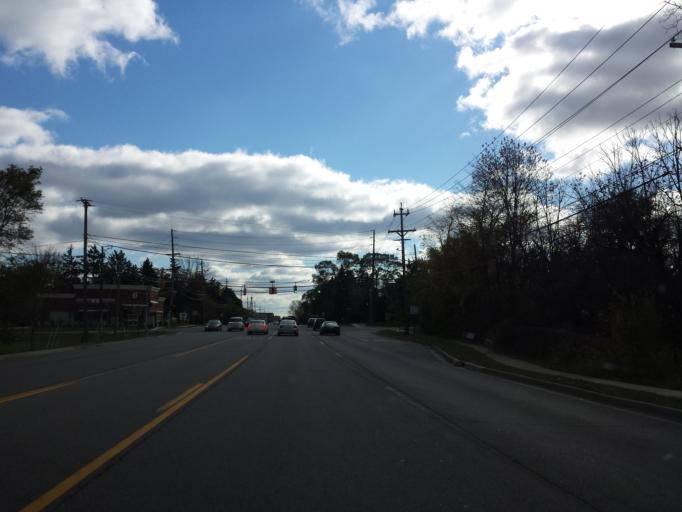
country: US
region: Michigan
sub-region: Oakland County
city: Troy
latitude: 42.5776
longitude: -83.1680
